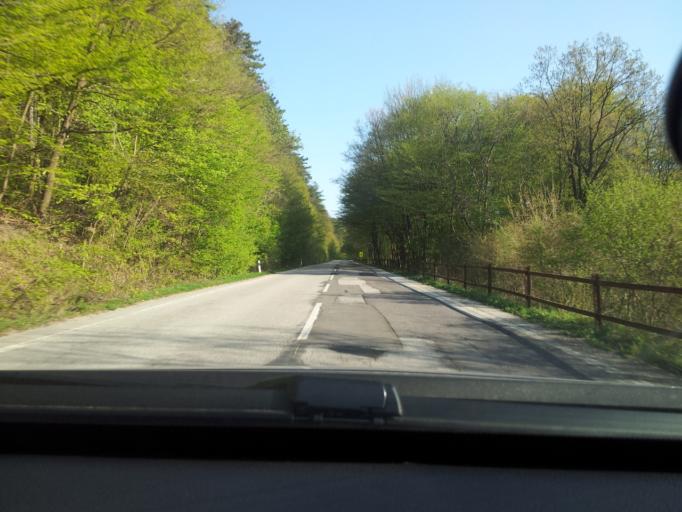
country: SK
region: Nitriansky
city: Zlate Moravce
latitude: 48.4690
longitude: 18.4117
